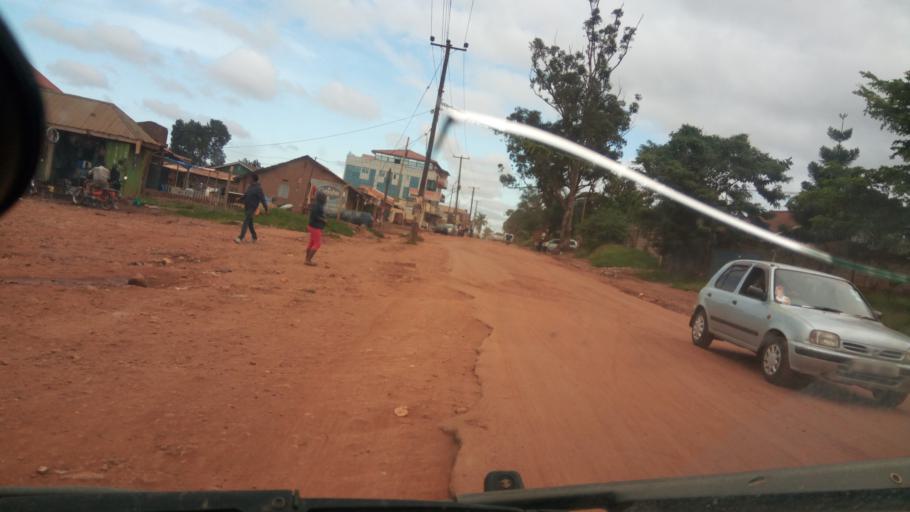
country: UG
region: Central Region
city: Kampala Central Division
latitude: 0.3242
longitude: 32.5611
